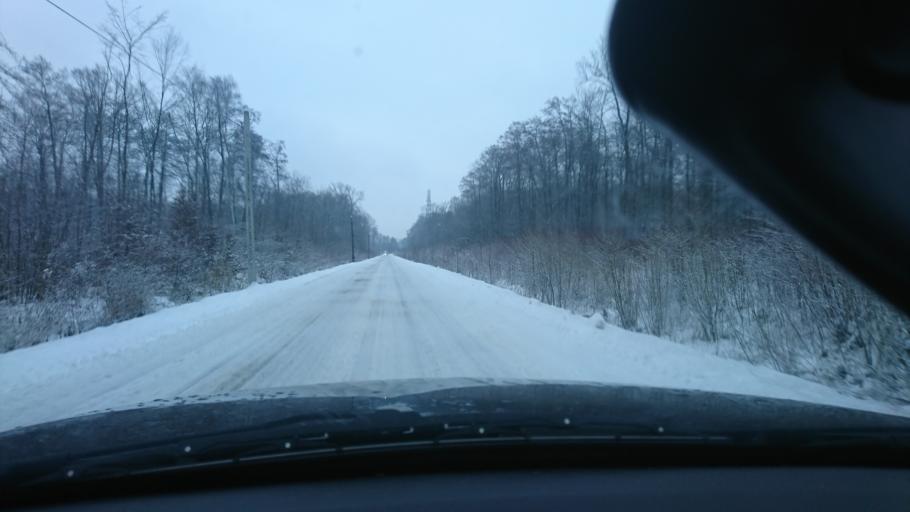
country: PL
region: Masovian Voivodeship
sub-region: Powiat ciechanowski
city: Glinojeck
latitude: 52.7481
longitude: 20.3086
